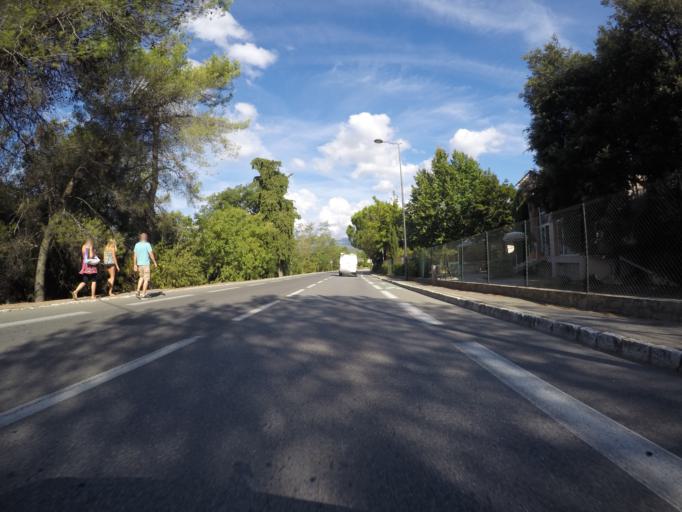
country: FR
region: Provence-Alpes-Cote d'Azur
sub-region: Departement des Alpes-Maritimes
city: Le Rouret
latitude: 43.6640
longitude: 7.0541
